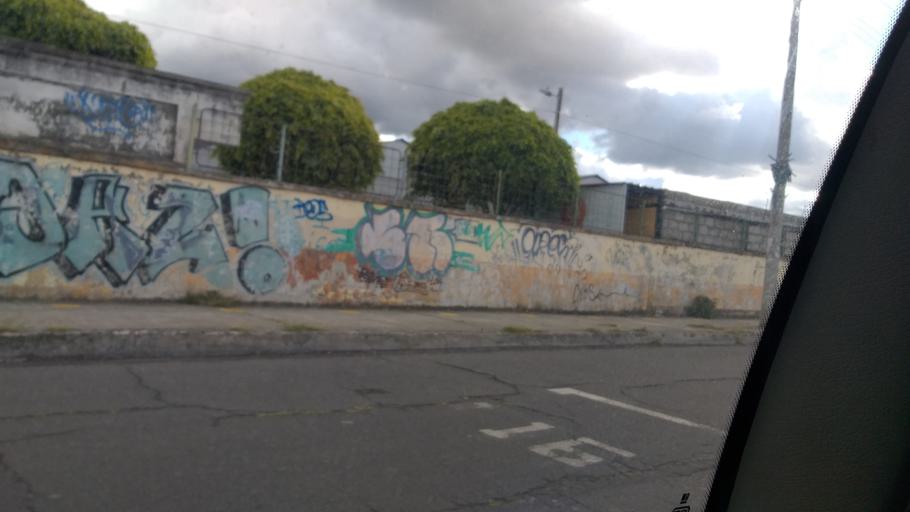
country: EC
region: Chimborazo
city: Riobamba
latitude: -1.6849
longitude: -78.6326
